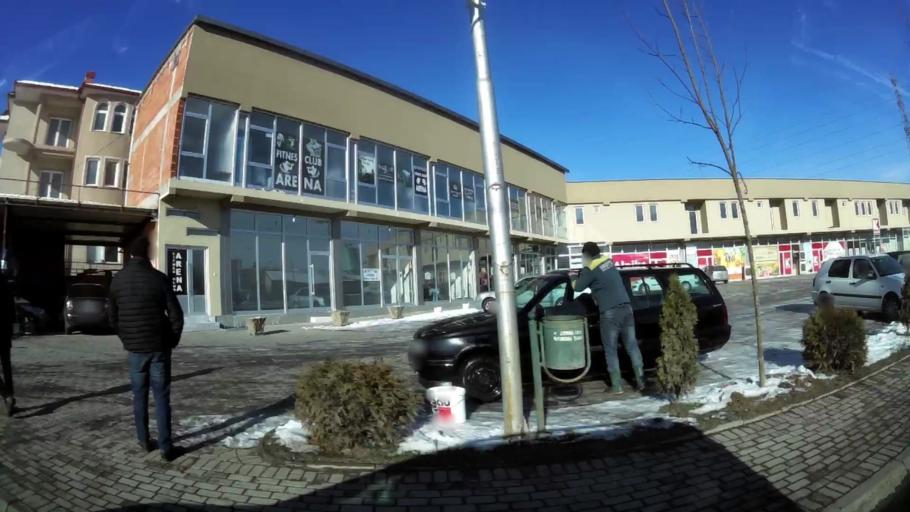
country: MK
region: Saraj
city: Saraj
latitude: 41.9949
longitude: 21.3217
